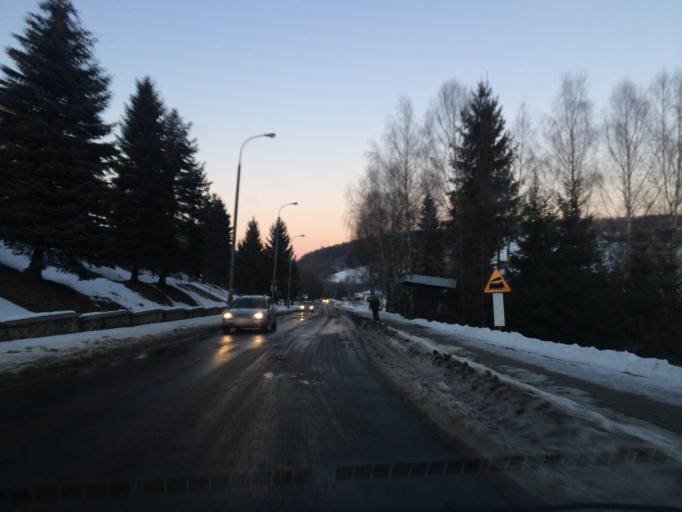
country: PL
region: Subcarpathian Voivodeship
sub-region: Powiat bieszczadzki
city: Ustrzyki Dolne
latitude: 49.4174
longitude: 22.5722
